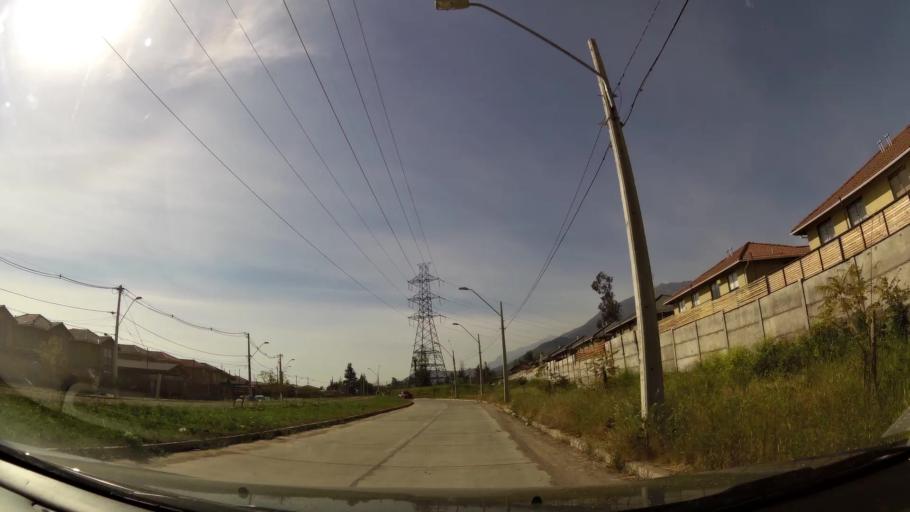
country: CL
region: Santiago Metropolitan
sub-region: Provincia de Cordillera
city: Puente Alto
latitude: -33.5963
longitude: -70.5412
